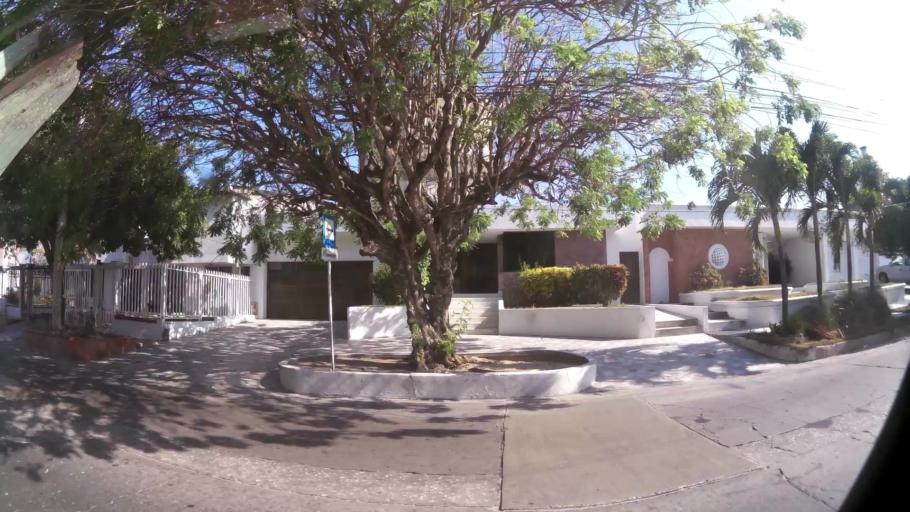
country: CO
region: Atlantico
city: Barranquilla
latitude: 10.9965
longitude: -74.8303
